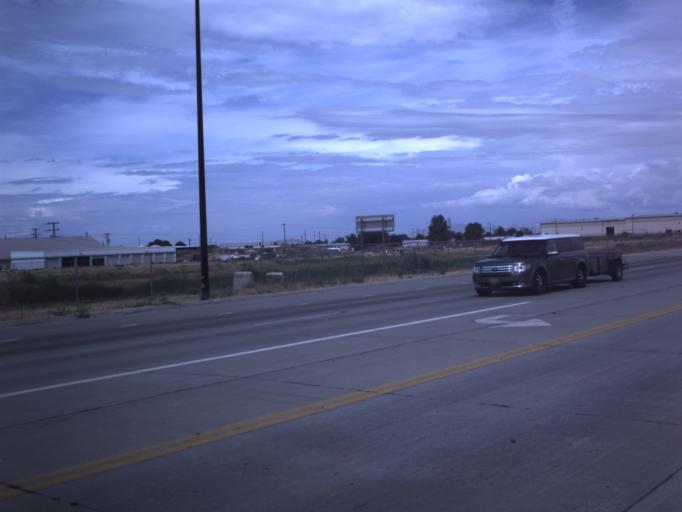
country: US
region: Utah
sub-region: Davis County
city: Clearfield
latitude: 41.1068
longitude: -112.0294
